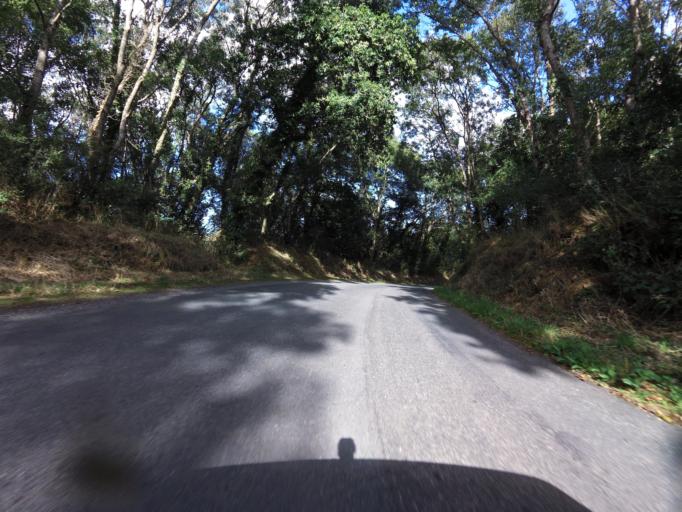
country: FR
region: Brittany
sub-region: Departement des Cotes-d'Armor
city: Plouha
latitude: 48.6742
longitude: -2.8926
